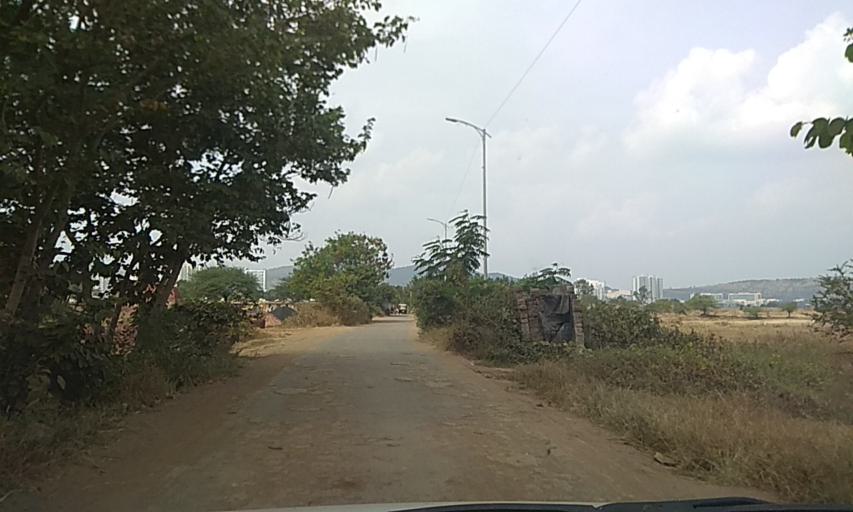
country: IN
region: Maharashtra
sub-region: Pune Division
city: Pimpri
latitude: 18.5800
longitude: 73.7078
